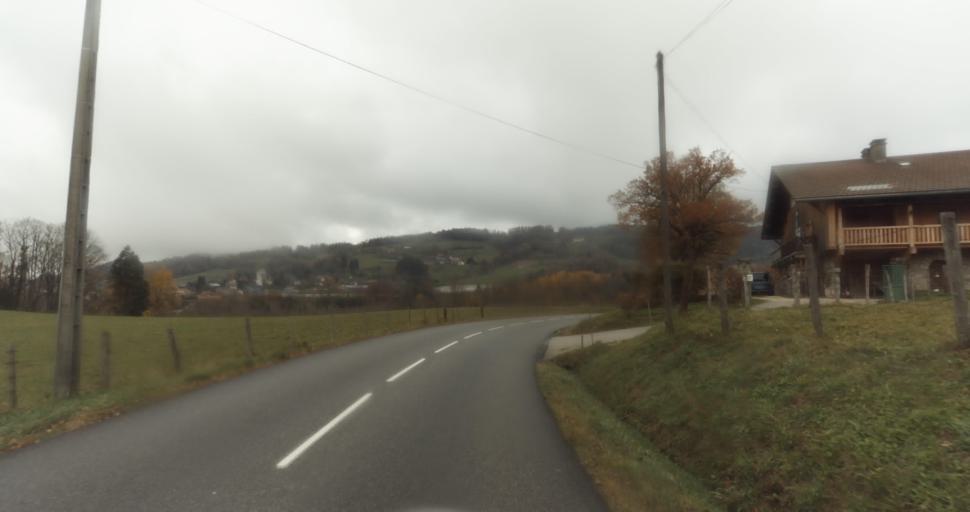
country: FR
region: Rhone-Alpes
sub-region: Departement de la Haute-Savoie
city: Thorens-Glieres
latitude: 45.9955
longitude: 6.2585
